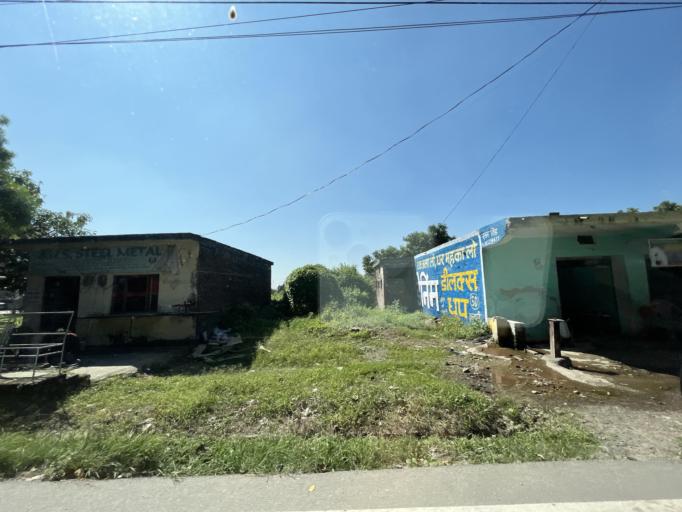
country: IN
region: Uttarakhand
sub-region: Naini Tal
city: Kaladhungi
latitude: 29.2875
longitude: 79.3447
